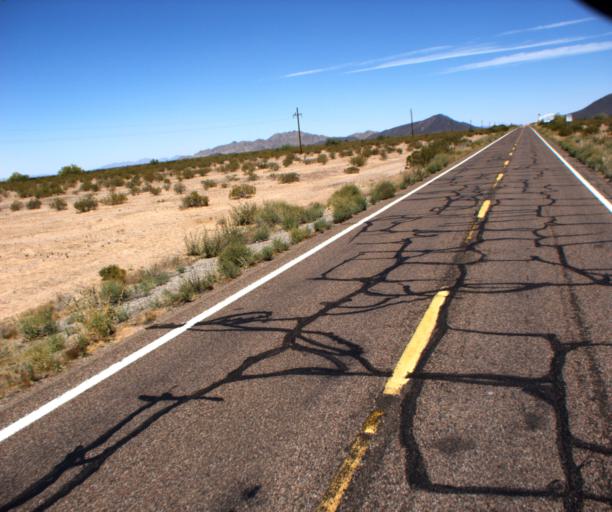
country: US
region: Arizona
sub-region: Maricopa County
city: Gila Bend
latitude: 32.7082
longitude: -112.8453
